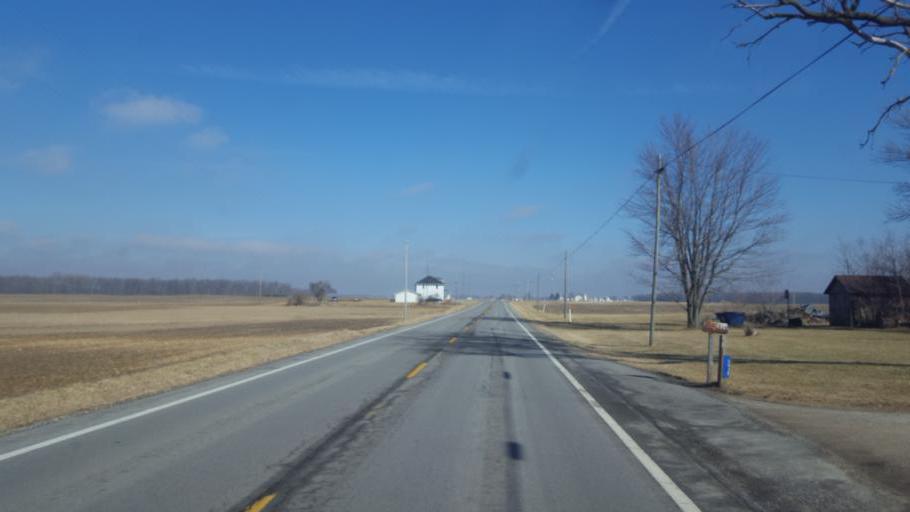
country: US
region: Ohio
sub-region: Crawford County
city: Bucyrus
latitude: 40.9189
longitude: -82.9522
